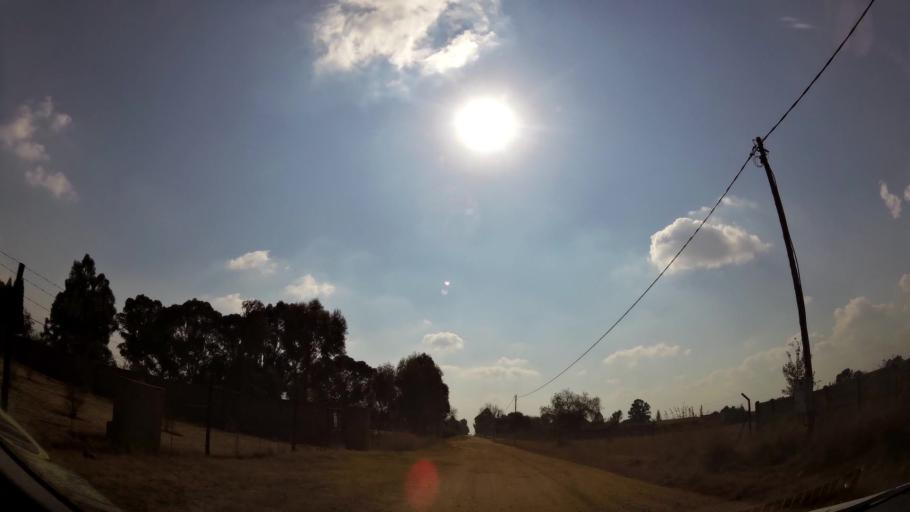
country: ZA
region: Gauteng
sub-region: Ekurhuleni Metropolitan Municipality
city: Springs
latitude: -26.1908
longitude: 28.5364
